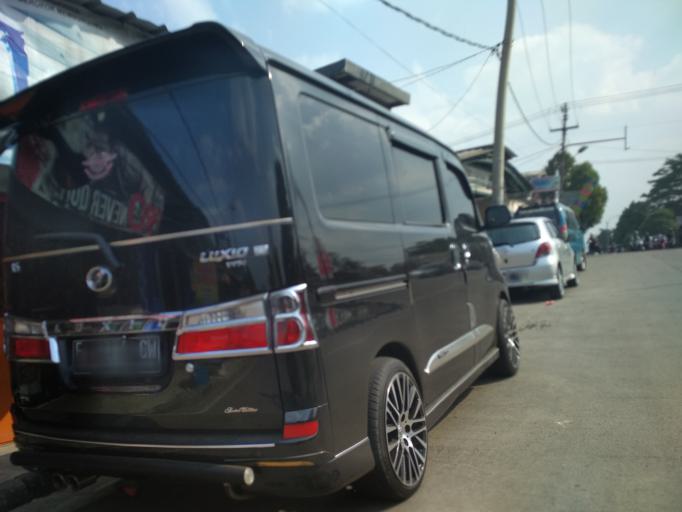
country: ID
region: West Java
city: Bogor
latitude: -6.5691
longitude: 106.7579
